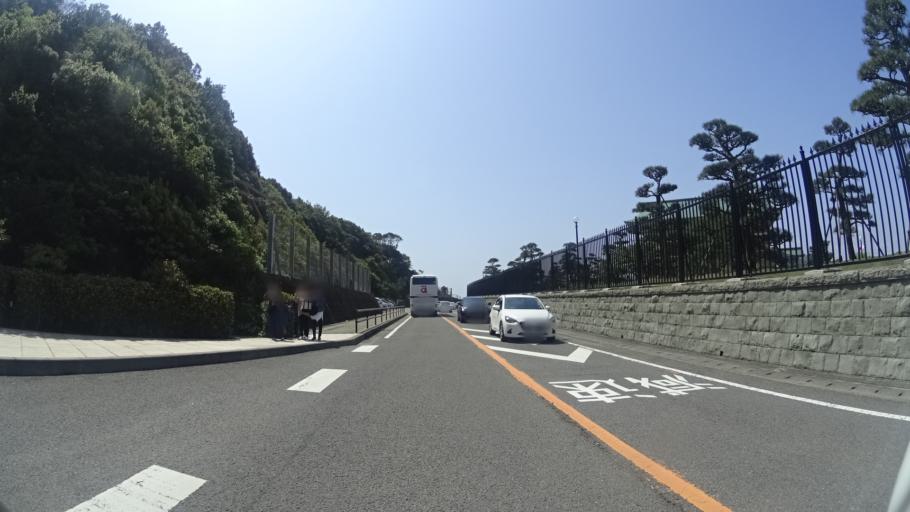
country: JP
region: Tokushima
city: Narutocho-mitsuishi
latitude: 34.2311
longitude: 134.6371
